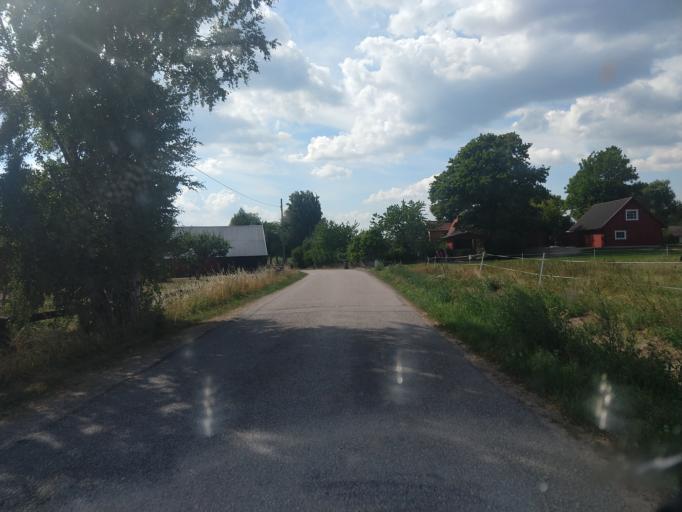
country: SE
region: Blekinge
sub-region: Karlskrona Kommun
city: Nattraby
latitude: 56.2485
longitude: 15.5338
